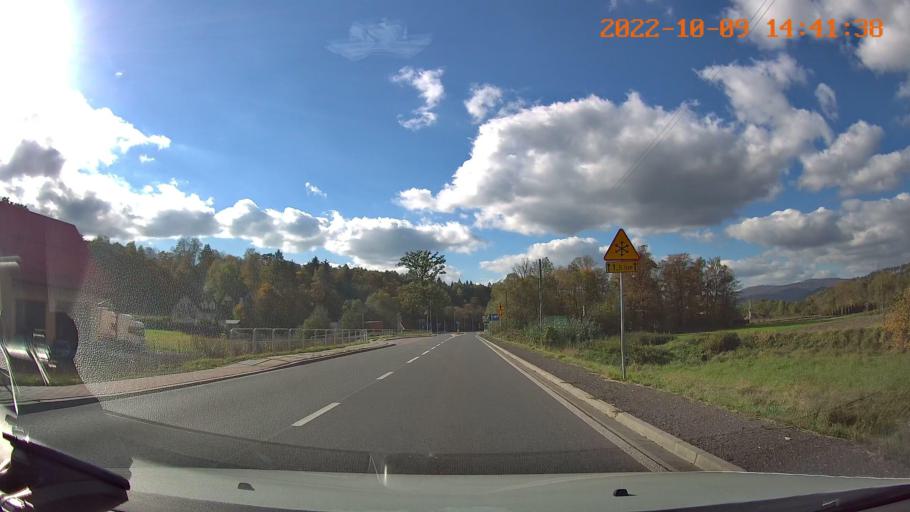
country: PL
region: Lesser Poland Voivodeship
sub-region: Powiat myslenicki
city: Lubien
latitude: 49.7101
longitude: 20.0107
